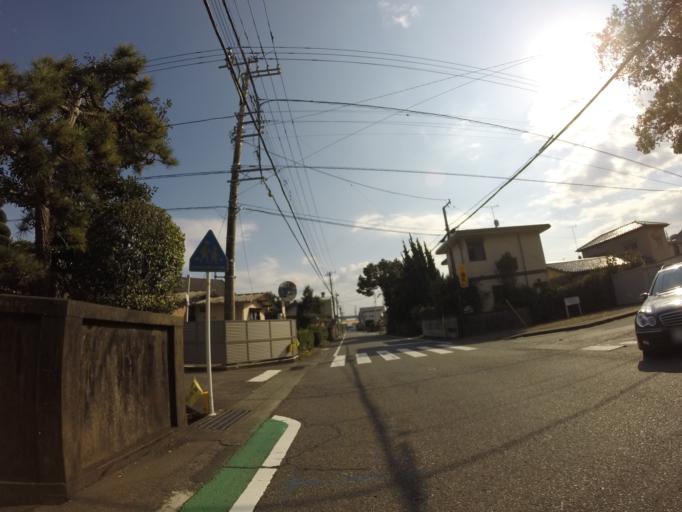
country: JP
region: Shizuoka
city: Fujinomiya
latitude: 35.2032
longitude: 138.6355
